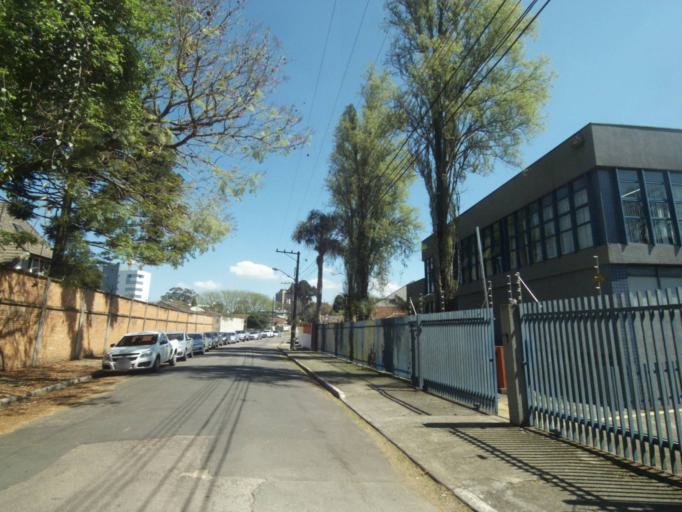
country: BR
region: Parana
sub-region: Curitiba
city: Curitiba
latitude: -25.4105
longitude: -49.2389
